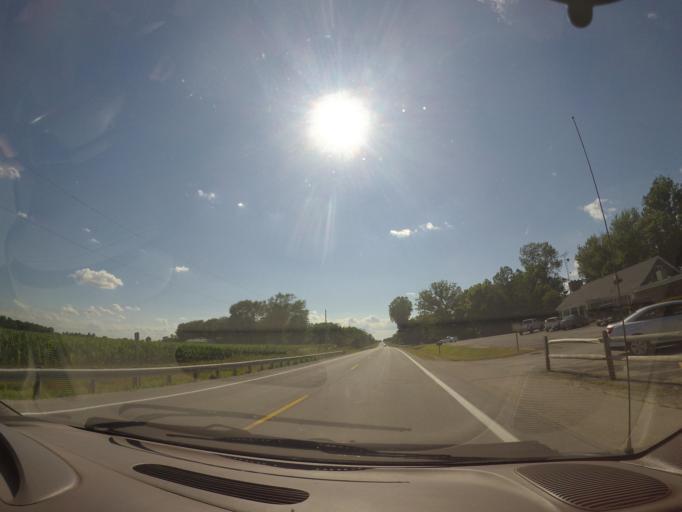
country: US
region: Ohio
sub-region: Sandusky County
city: Stony Prairie
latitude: 41.3422
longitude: -83.1858
